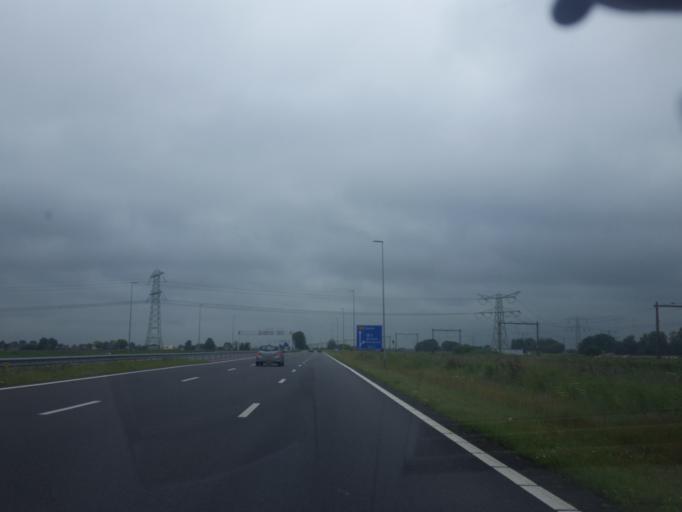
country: NL
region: Friesland
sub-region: Gemeente Leeuwarden
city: Wirdum
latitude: 53.1542
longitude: 5.7916
